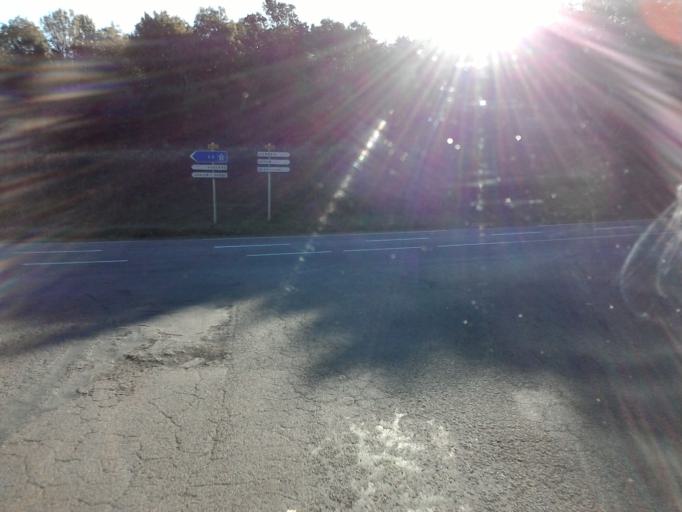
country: FR
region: Bourgogne
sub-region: Departement de la Cote-d'Or
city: Saulieu
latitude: 47.2724
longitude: 4.2367
